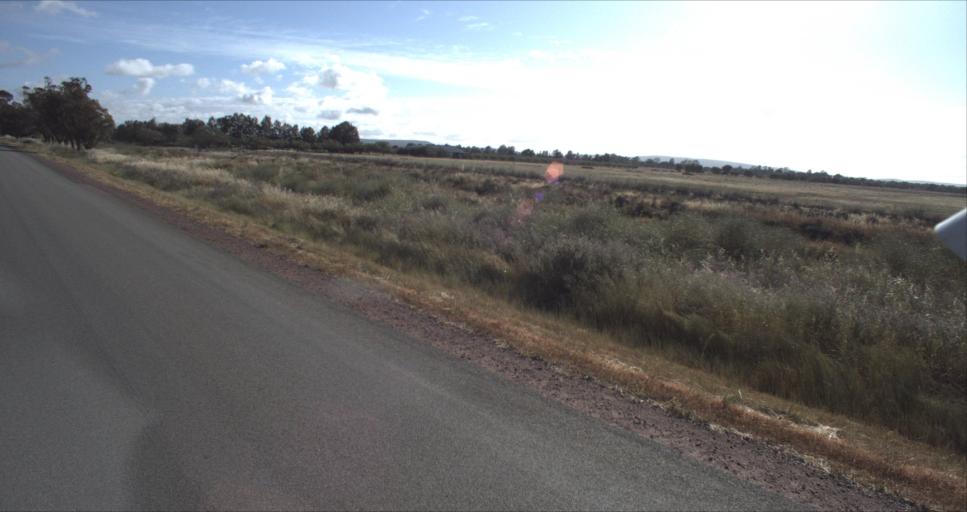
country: AU
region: New South Wales
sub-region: Leeton
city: Leeton
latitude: -34.5228
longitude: 146.3903
